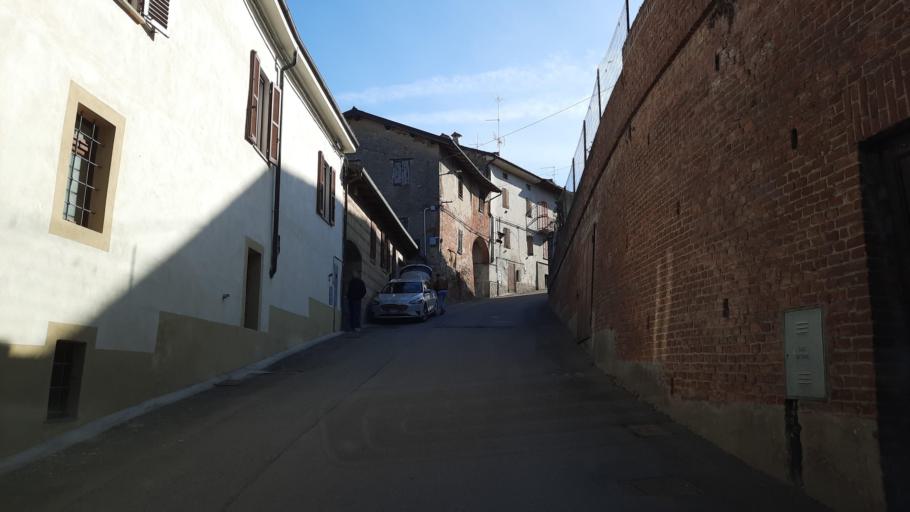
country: IT
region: Piedmont
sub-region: Provincia di Alessandria
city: Camagna Monferrato
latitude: 45.0194
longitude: 8.4330
